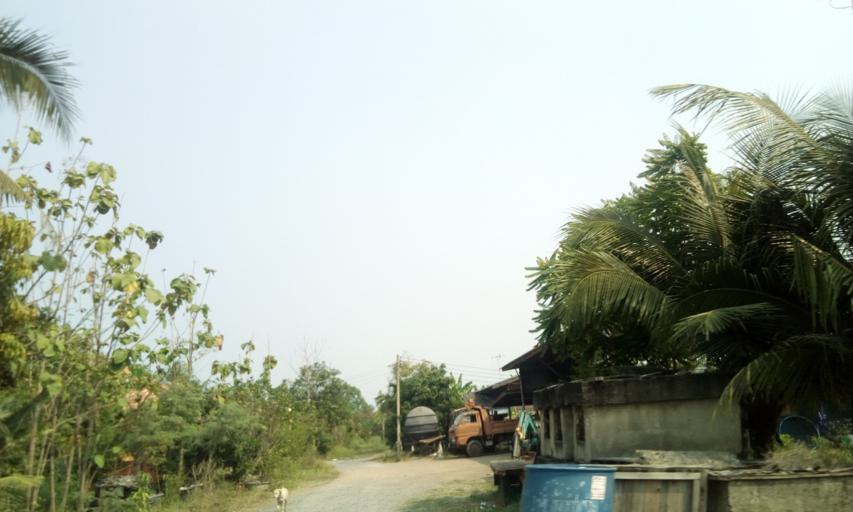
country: TH
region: Pathum Thani
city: Lam Luk Ka
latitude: 13.9423
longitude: 100.7242
